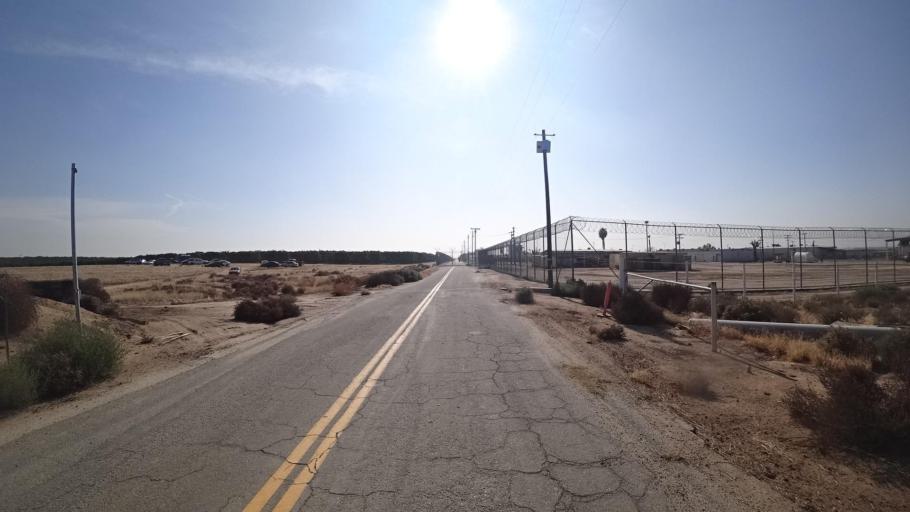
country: US
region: California
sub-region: Kern County
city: Oildale
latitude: 35.5151
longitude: -119.1087
